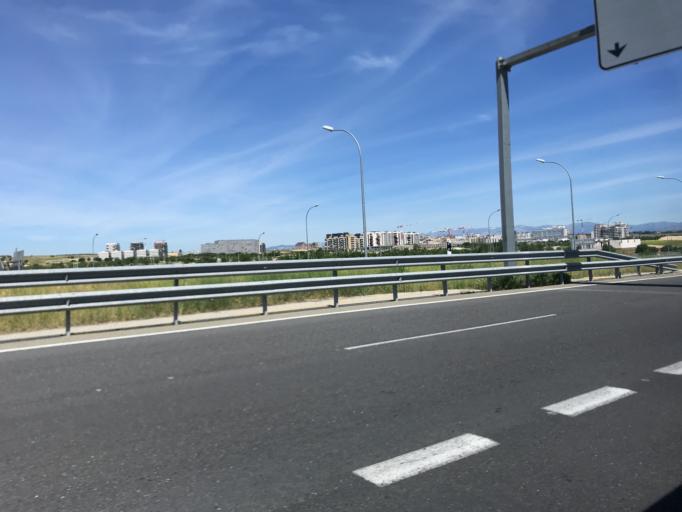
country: ES
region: Madrid
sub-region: Provincia de Madrid
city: Barajas de Madrid
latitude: 40.4822
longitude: -3.6011
